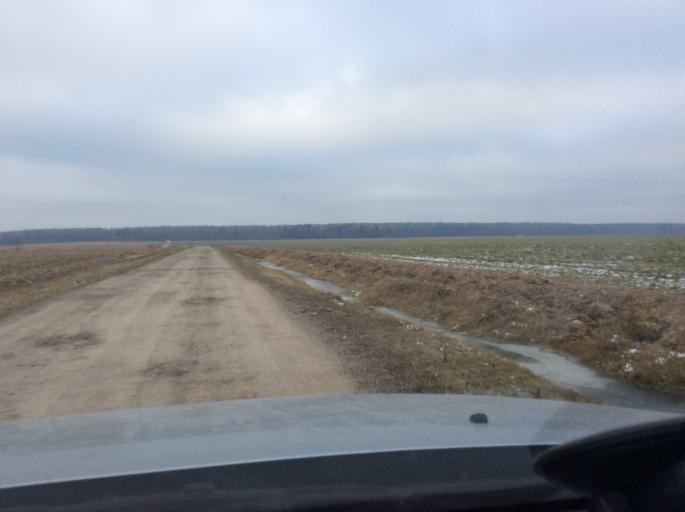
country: RU
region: Moskovskaya
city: Troitsk
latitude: 55.3596
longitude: 37.1922
